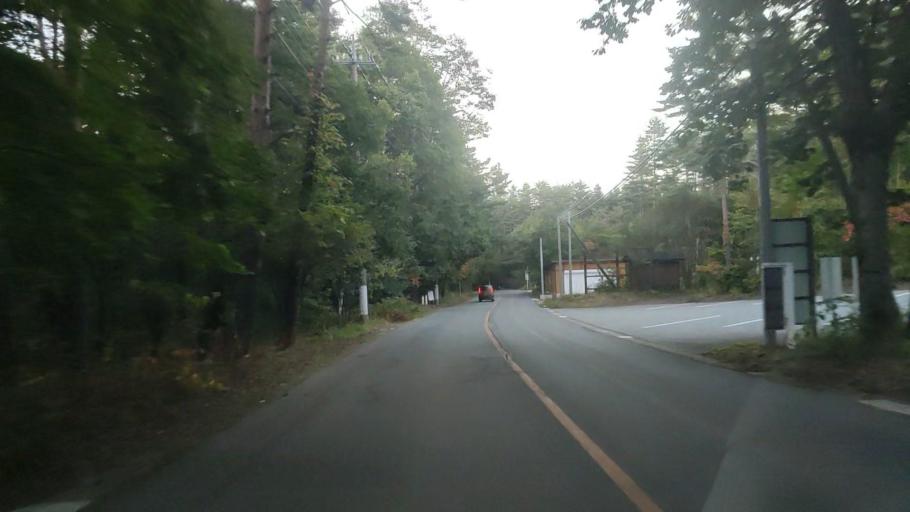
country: JP
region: Nagano
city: Komoro
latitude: 36.4437
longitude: 138.5791
